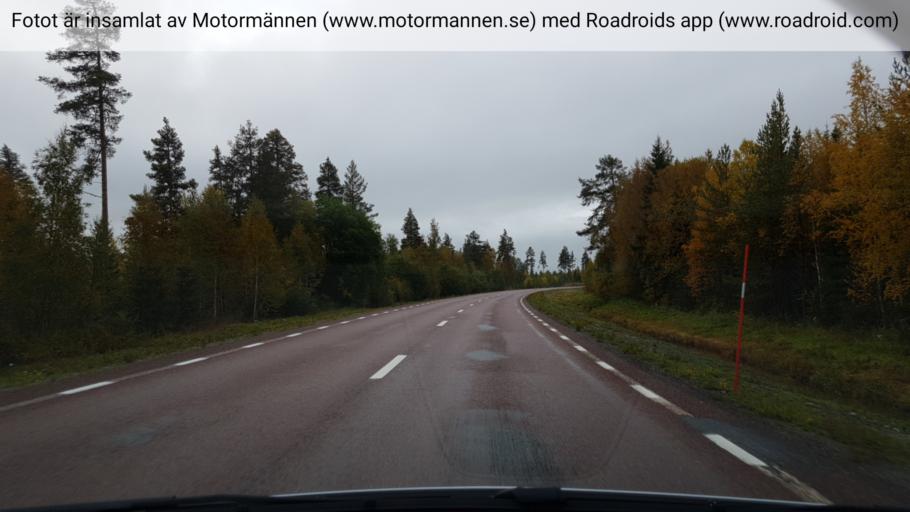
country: SE
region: Vaesterbotten
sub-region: Dorotea Kommun
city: Dorotea
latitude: 64.2224
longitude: 16.2976
